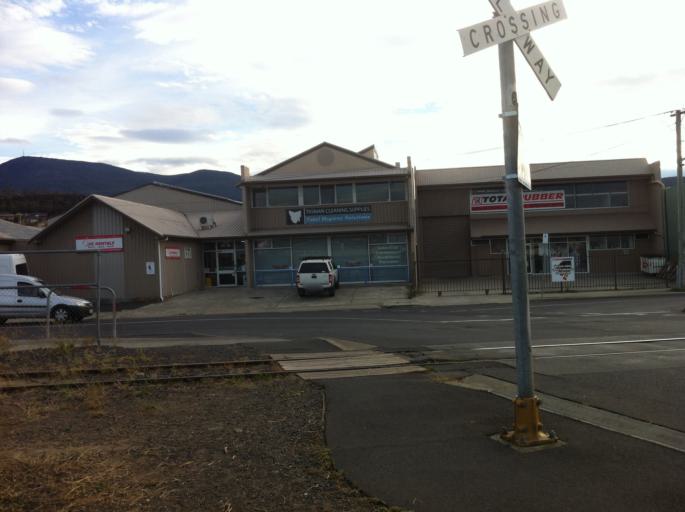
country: AU
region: Tasmania
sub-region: Glenorchy
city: Moonah
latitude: -42.8429
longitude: 147.2951
